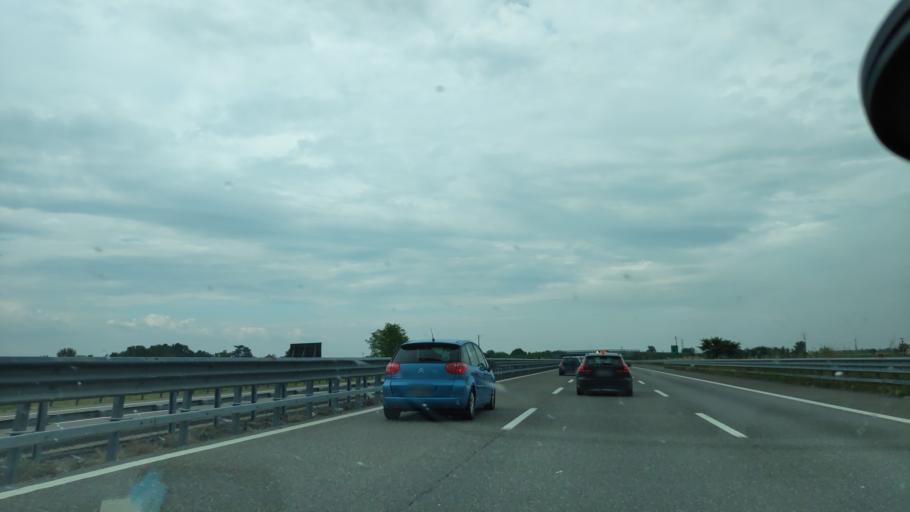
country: IT
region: Piedmont
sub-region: Provincia di Alessandria
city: Castelnuovo Scrivia
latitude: 44.9639
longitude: 8.8836
